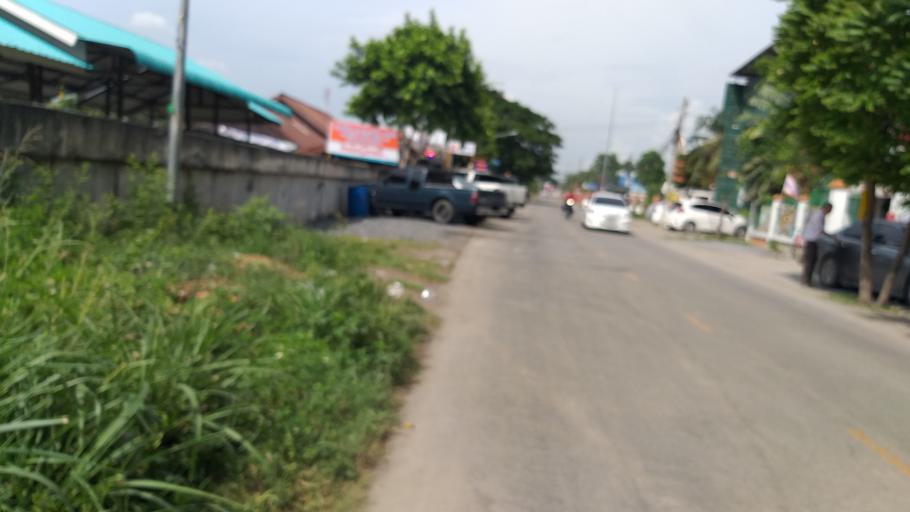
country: TH
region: Pathum Thani
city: Thanyaburi
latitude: 13.9956
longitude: 100.6701
